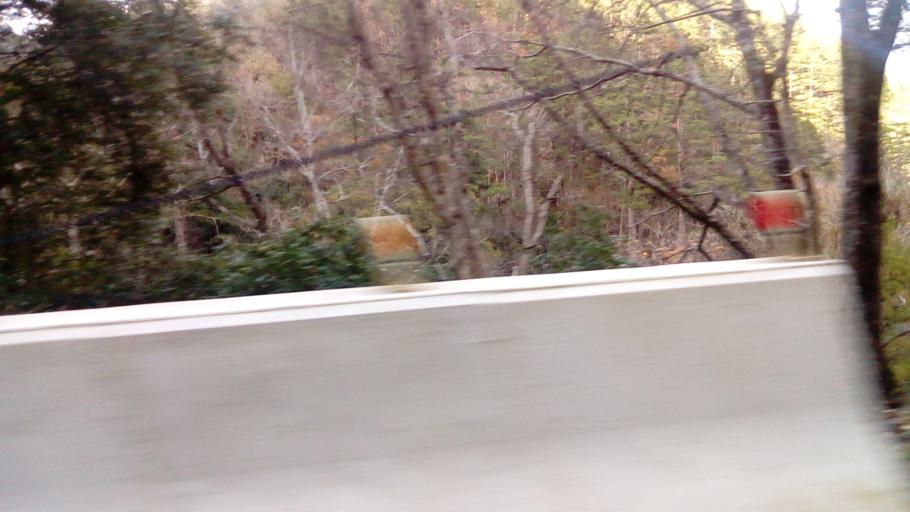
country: TW
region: Taiwan
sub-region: Hualien
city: Hualian
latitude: 24.3431
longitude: 121.3115
